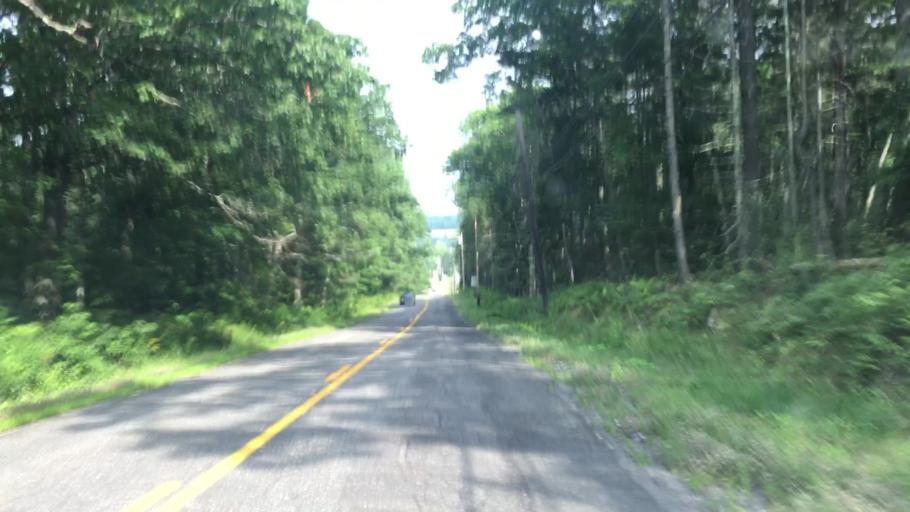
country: US
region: Maine
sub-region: Lincoln County
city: Waldoboro
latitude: 44.0965
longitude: -69.3928
